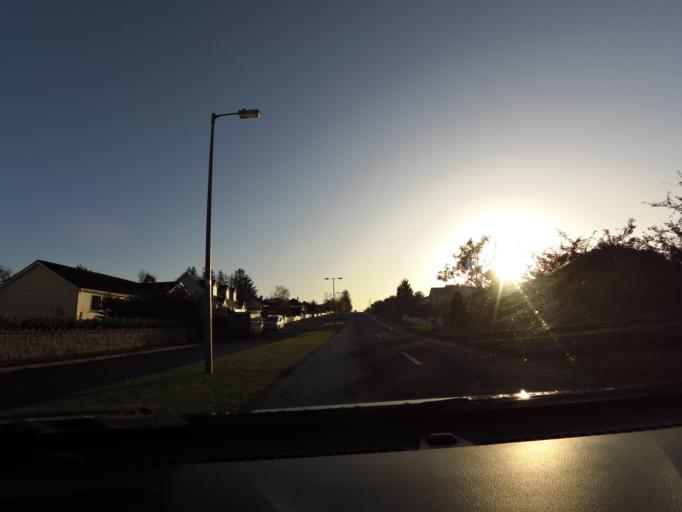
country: IE
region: Connaught
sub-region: Roscommon
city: Castlerea
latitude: 53.7595
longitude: -8.5137
